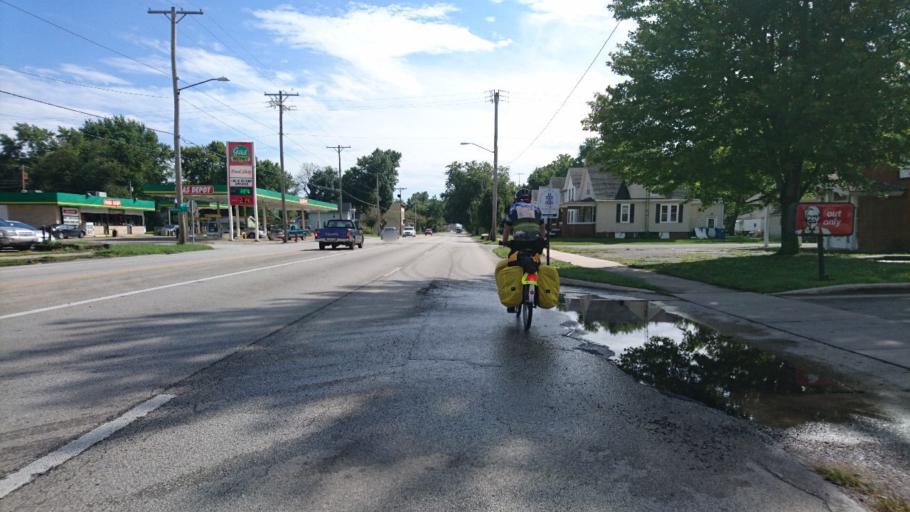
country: US
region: Illinois
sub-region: Sangamon County
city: Springfield
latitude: 39.8144
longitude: -89.6433
